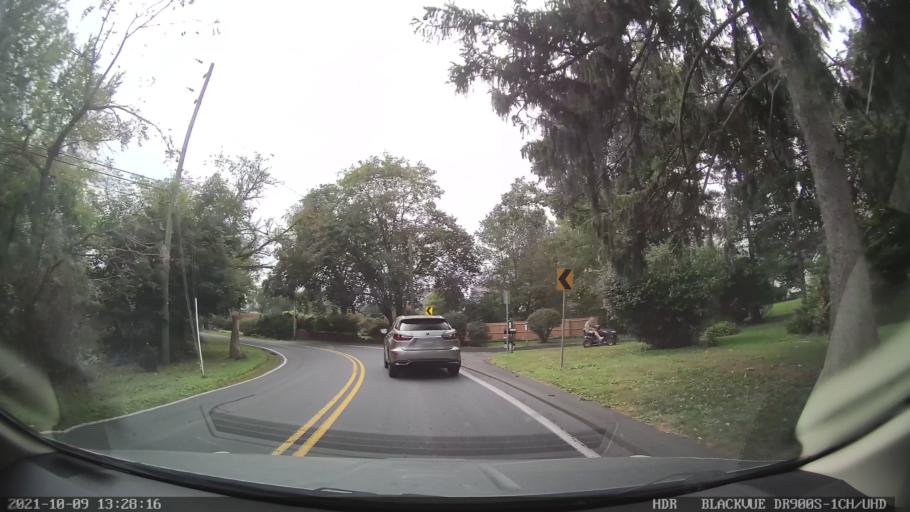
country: US
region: Pennsylvania
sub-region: Lehigh County
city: Ancient Oaks
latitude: 40.5411
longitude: -75.5921
